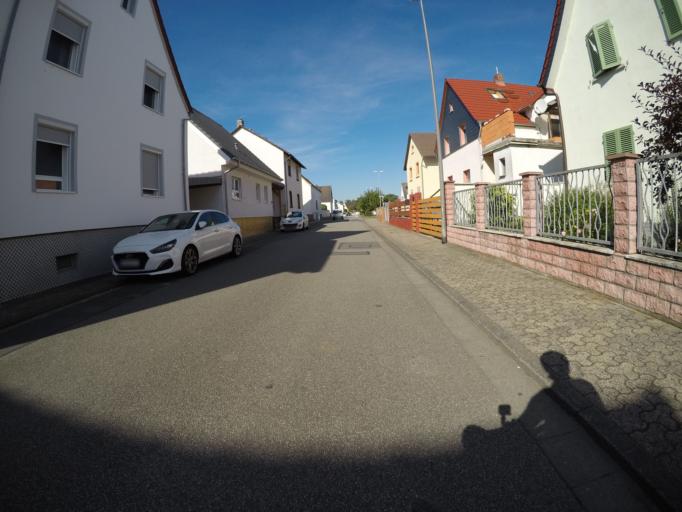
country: DE
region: Hesse
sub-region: Regierungsbezirk Darmstadt
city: Stockstadt am Rhein
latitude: 49.8101
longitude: 8.4711
